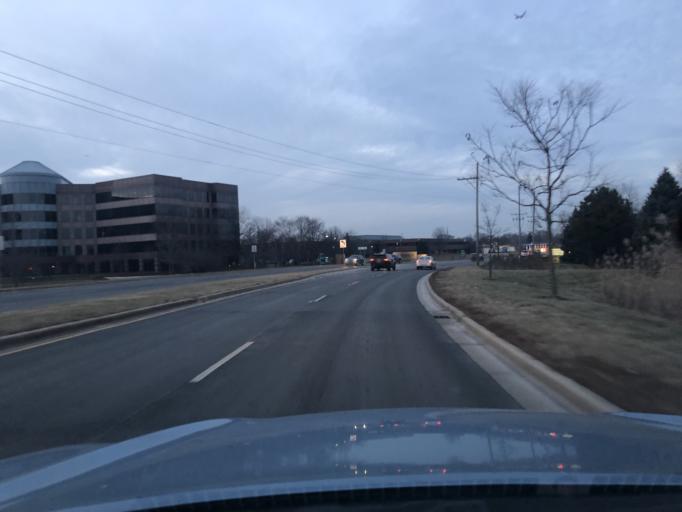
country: US
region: Illinois
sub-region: DuPage County
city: Itasca
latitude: 41.9887
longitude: -88.0028
